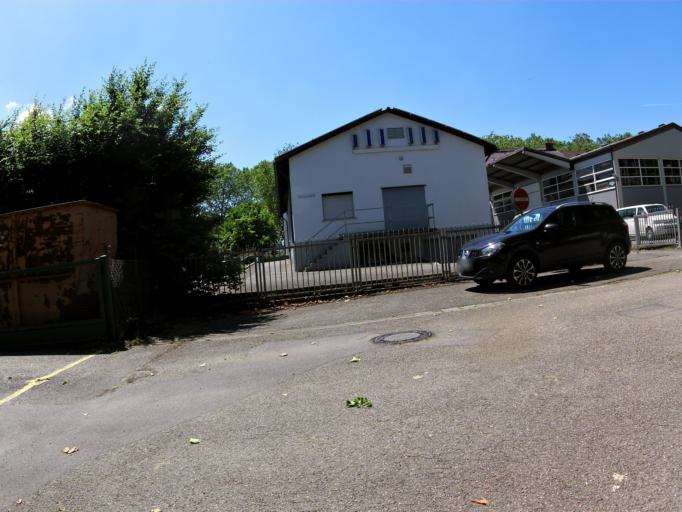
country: DE
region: Baden-Wuerttemberg
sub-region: Freiburg Region
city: Lahr
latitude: 48.3399
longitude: 7.8413
